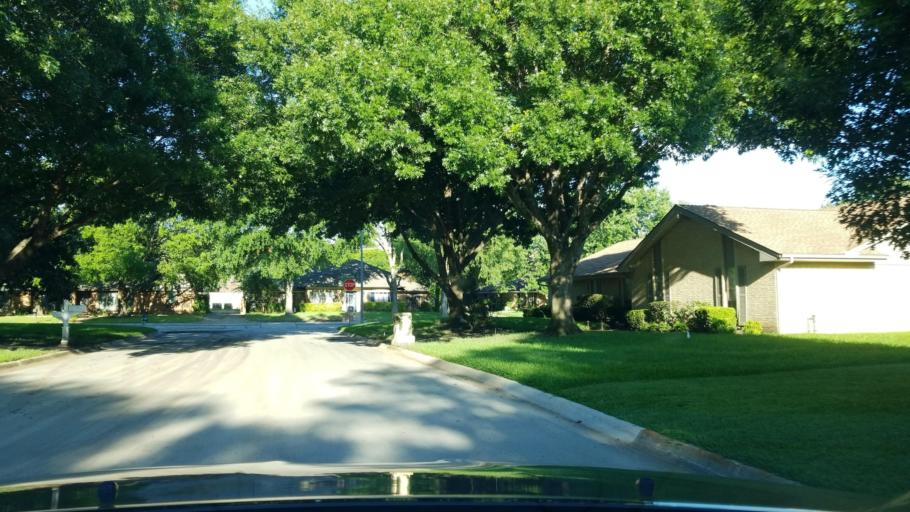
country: US
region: Texas
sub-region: Denton County
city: Denton
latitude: 33.2453
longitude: -97.1070
